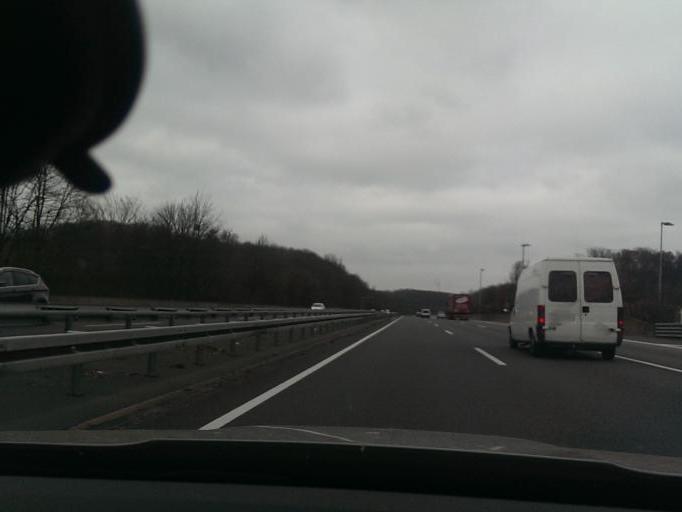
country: DE
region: Lower Saxony
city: Pohle
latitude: 52.2614
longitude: 9.3127
